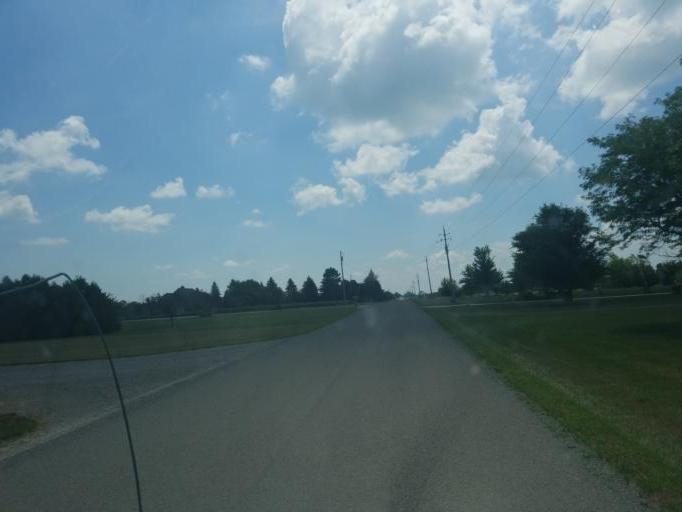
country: US
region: Ohio
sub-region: Mercer County
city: Celina
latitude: 40.5743
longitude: -84.4939
